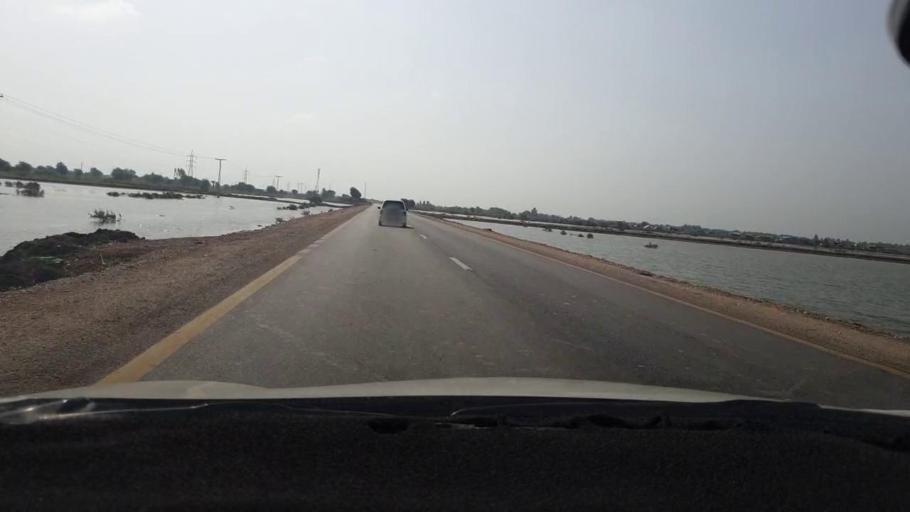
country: PK
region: Sindh
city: Jhol
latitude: 25.8934
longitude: 69.0281
